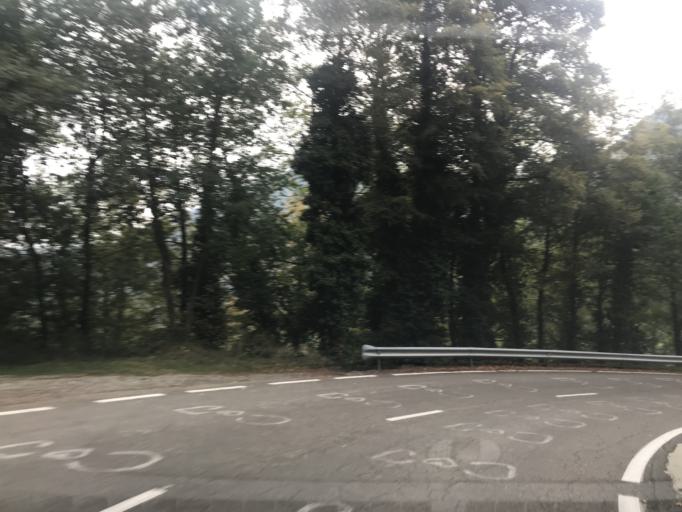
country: ES
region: Catalonia
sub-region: Provincia de Lleida
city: Les
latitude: 42.7797
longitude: 0.6829
